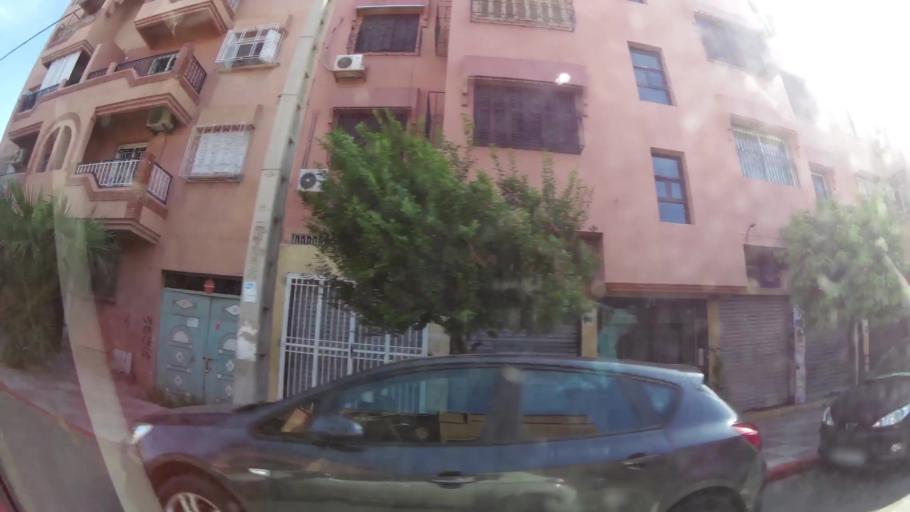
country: MA
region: Marrakech-Tensift-Al Haouz
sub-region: Marrakech
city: Marrakesh
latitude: 31.6447
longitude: -8.0036
